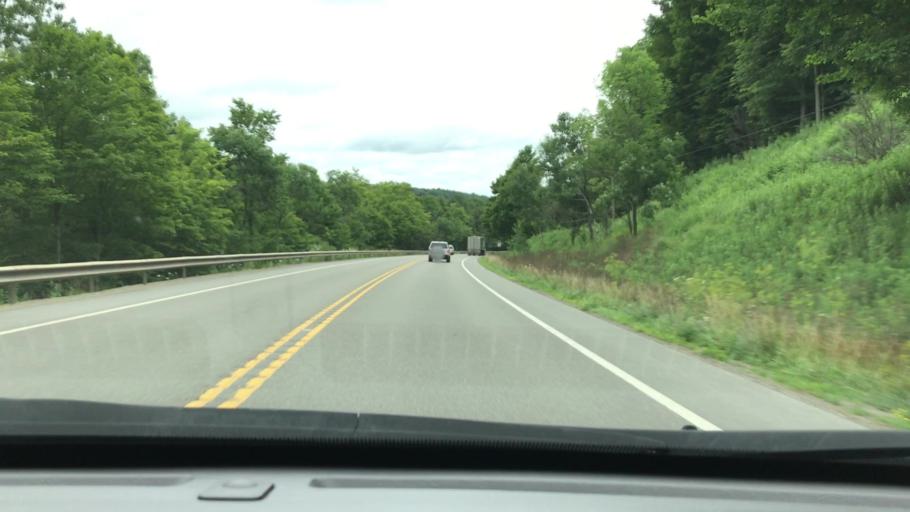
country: US
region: Pennsylvania
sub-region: McKean County
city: Kane
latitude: 41.6761
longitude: -78.6846
